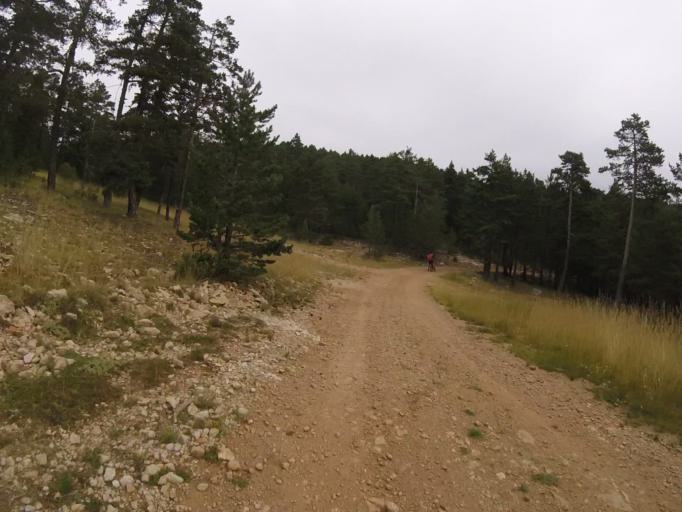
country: ES
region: Aragon
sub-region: Provincia de Teruel
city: Valdelinares
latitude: 40.3607
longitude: -0.6119
